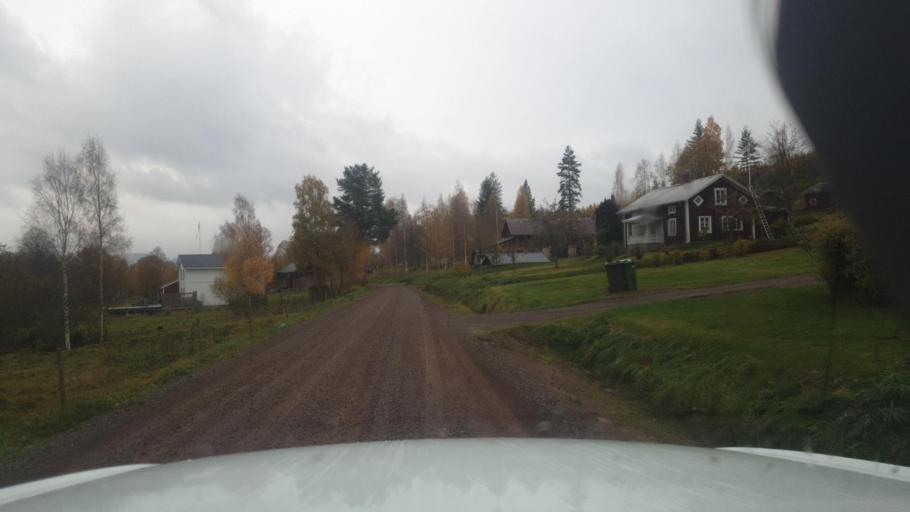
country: SE
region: Vaermland
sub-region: Torsby Kommun
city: Torsby
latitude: 59.9716
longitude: 12.8639
